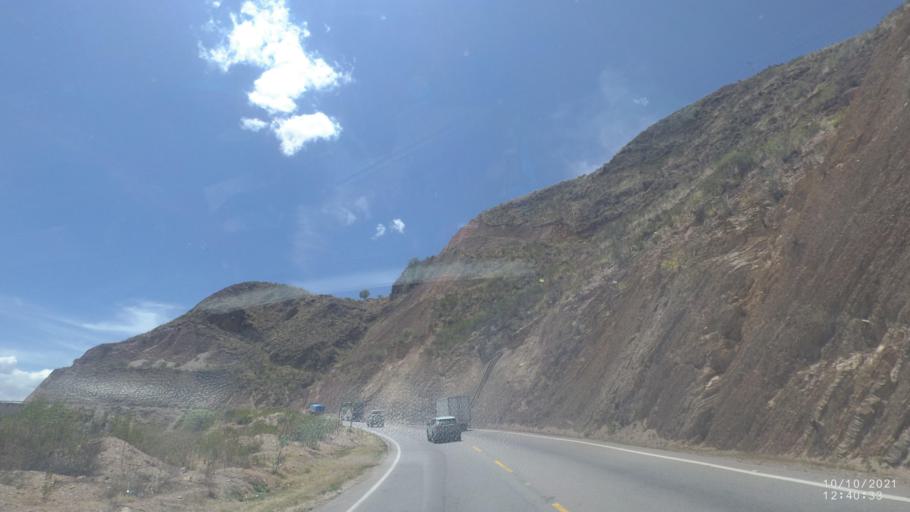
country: BO
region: Cochabamba
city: Irpa Irpa
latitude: -17.6399
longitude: -66.3882
